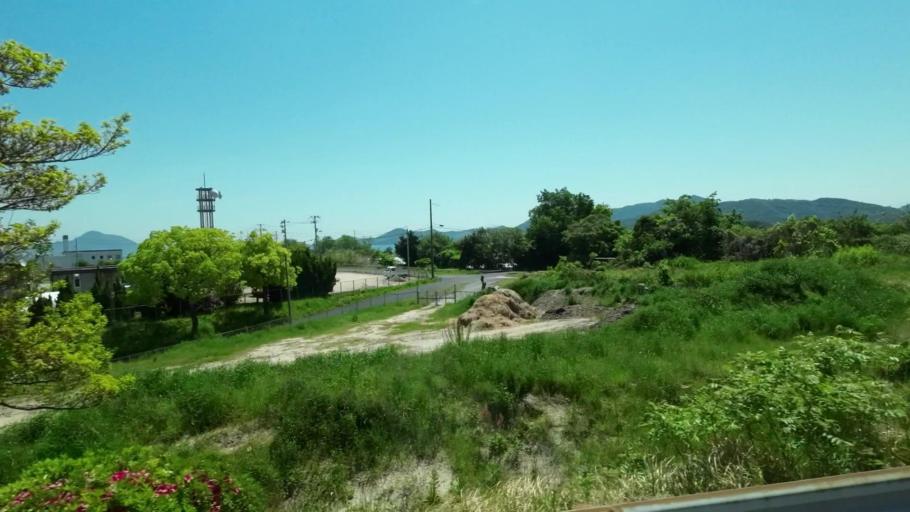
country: JP
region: Hiroshima
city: Innoshima
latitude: 34.2514
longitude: 133.0514
